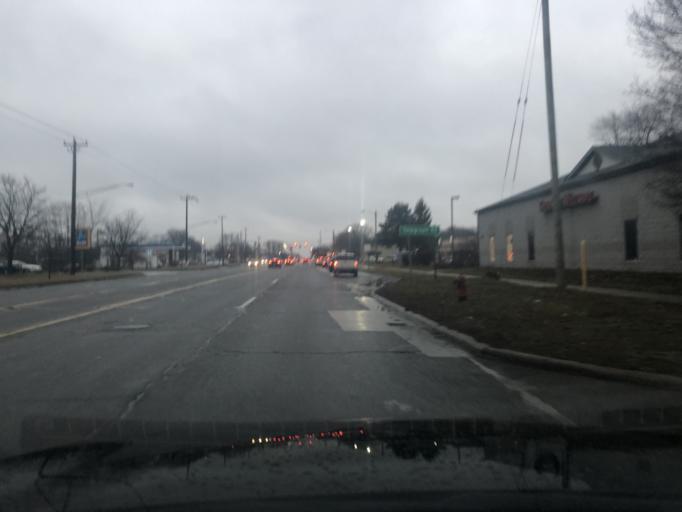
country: US
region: Michigan
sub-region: Wayne County
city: Taylor
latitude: 42.2690
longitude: -83.2728
